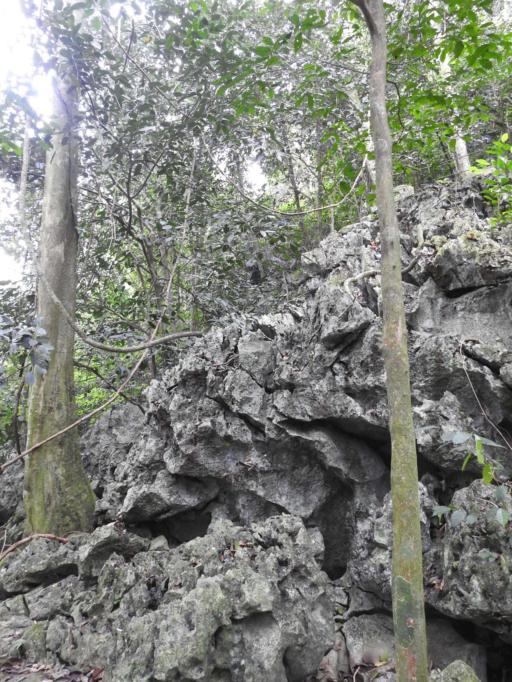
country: VN
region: Ninh Binh
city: Thi Tran Nho Quan
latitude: 20.2933
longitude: 105.6685
